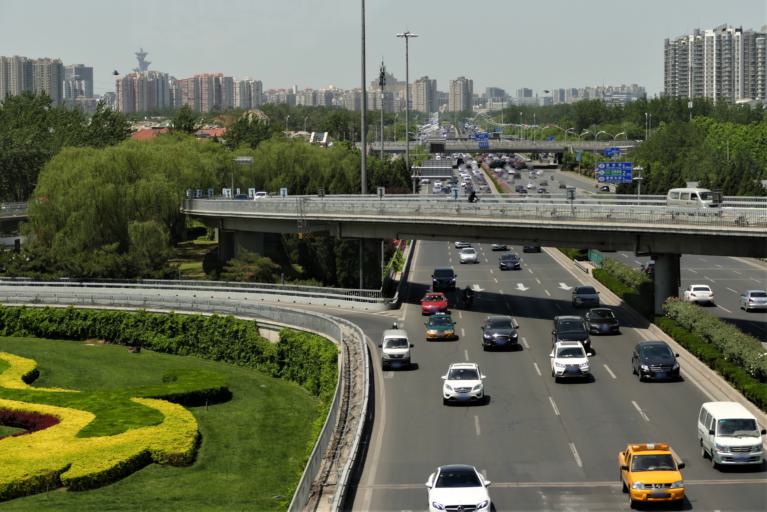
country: CN
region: Beijing
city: Wangjing
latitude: 39.9701
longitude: 116.4630
